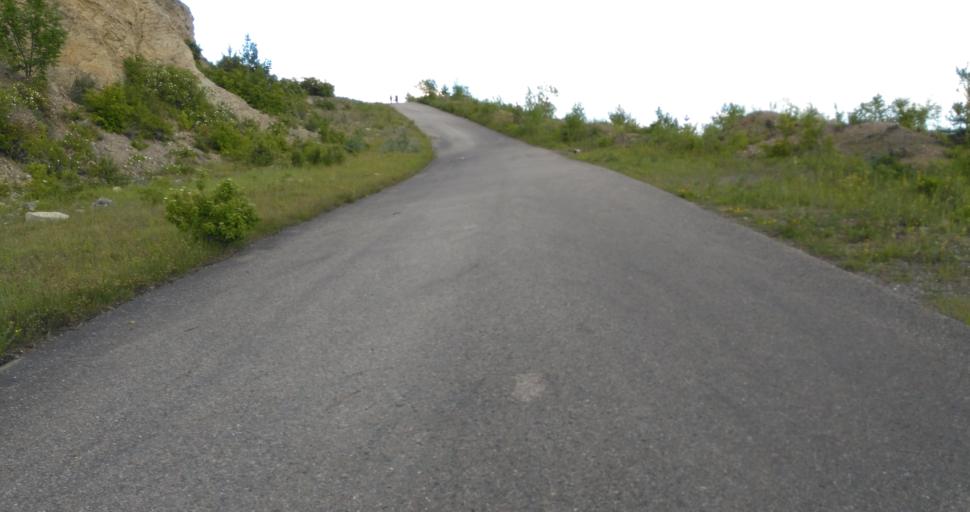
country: CZ
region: South Moravian
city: Bilovice nad Svitavou
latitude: 49.2205
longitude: 16.6690
